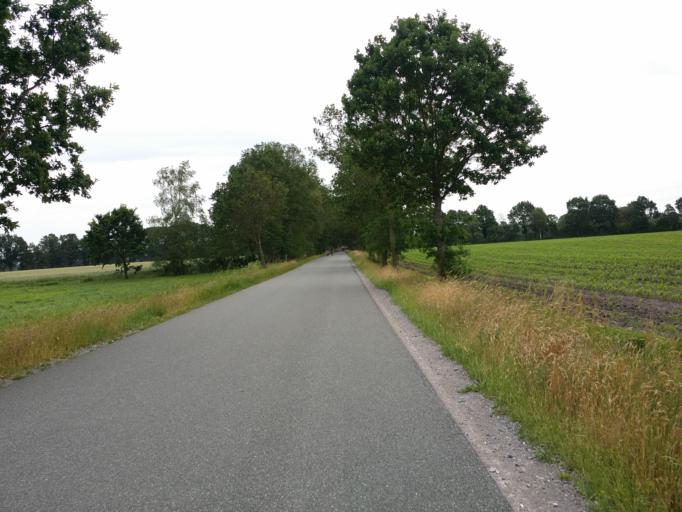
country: DE
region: Lower Saxony
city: Bockhorn
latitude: 53.3508
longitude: 8.0213
